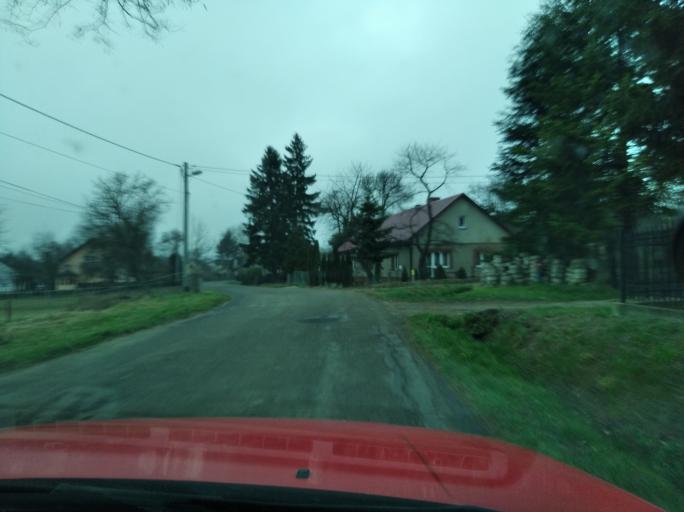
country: PL
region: Subcarpathian Voivodeship
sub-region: Powiat przeworski
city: Mirocin
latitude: 50.0467
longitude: 22.5521
